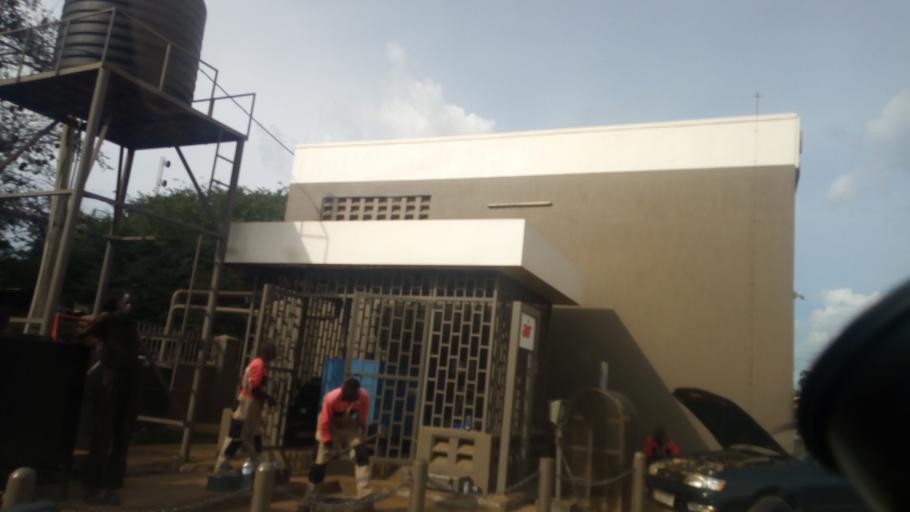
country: UG
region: Northern Region
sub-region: Lira District
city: Lira
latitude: 2.2346
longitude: 32.8926
